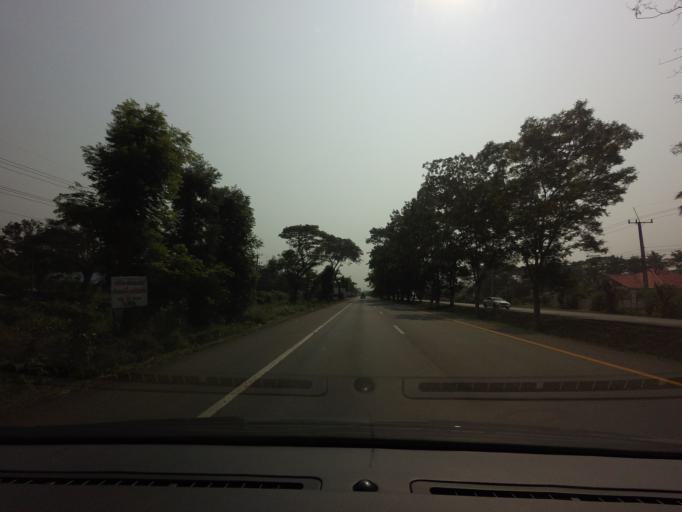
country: TH
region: Prachuap Khiri Khan
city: Sam Roi Yot
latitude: 12.1788
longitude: 99.8470
